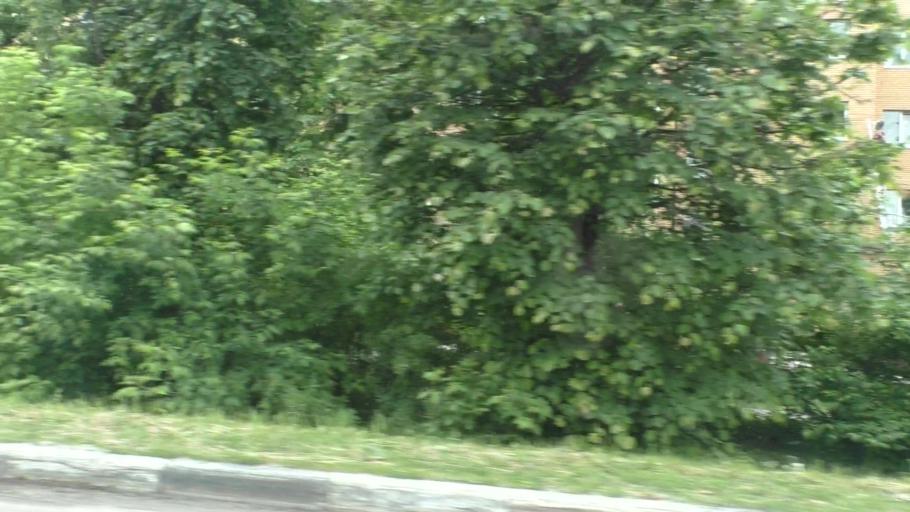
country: RU
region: Moskovskaya
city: Yegor'yevsk
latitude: 55.3932
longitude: 39.0206
